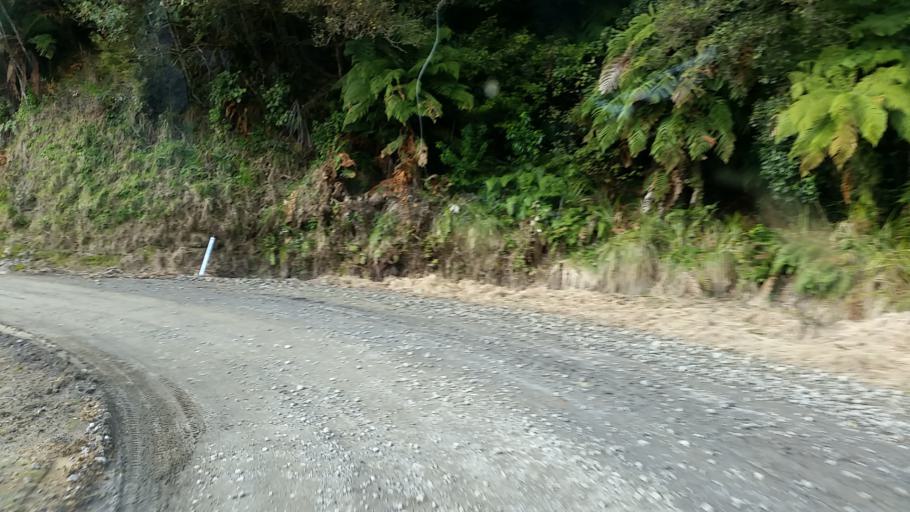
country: NZ
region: Taranaki
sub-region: New Plymouth District
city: Waitara
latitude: -39.1567
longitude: 174.5574
